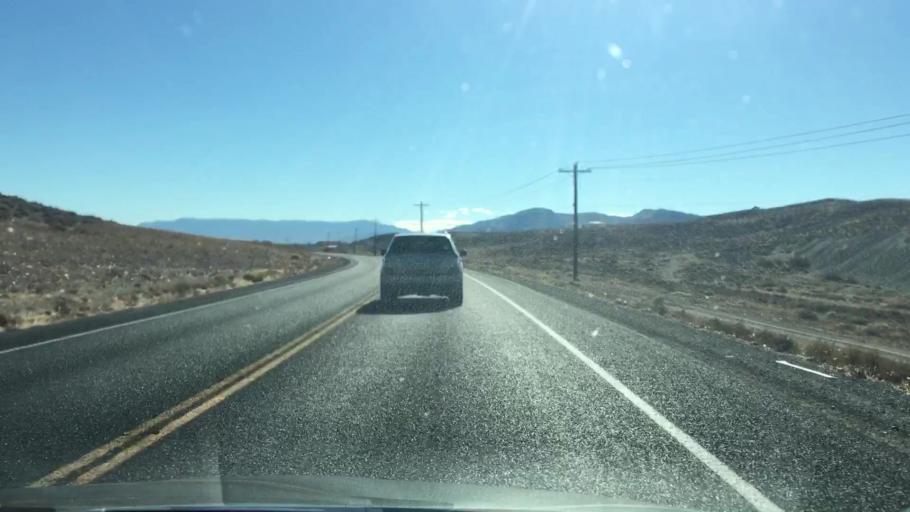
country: US
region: Nevada
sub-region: Lyon County
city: Yerington
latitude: 39.0112
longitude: -119.1829
